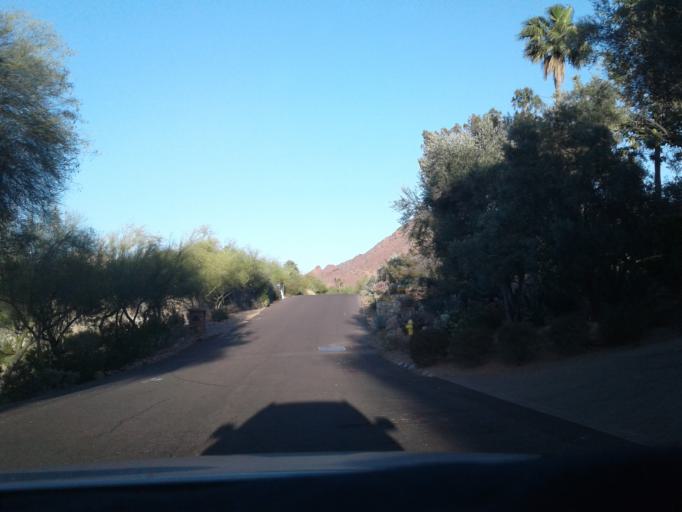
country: US
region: Arizona
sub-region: Maricopa County
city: Paradise Valley
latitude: 33.5272
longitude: -111.9904
